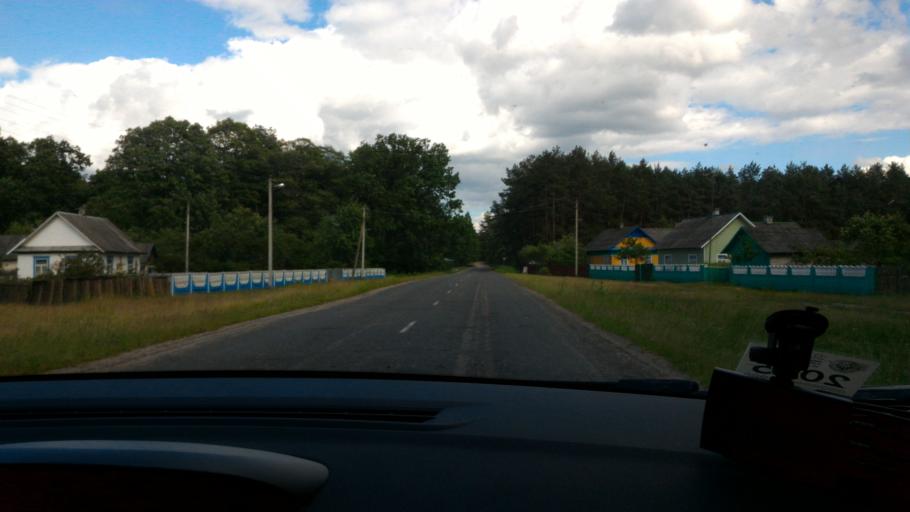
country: BY
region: Brest
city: Ivatsevichy
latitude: 52.7844
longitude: 25.6561
